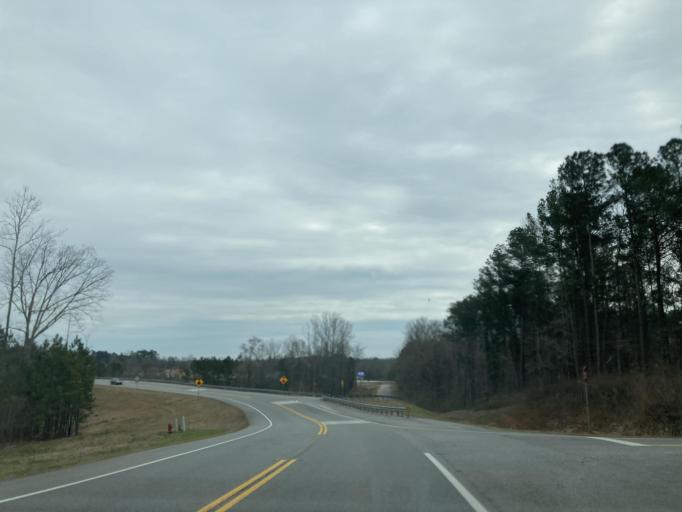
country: US
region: Georgia
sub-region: Jones County
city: Gray
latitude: 32.9905
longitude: -83.5754
